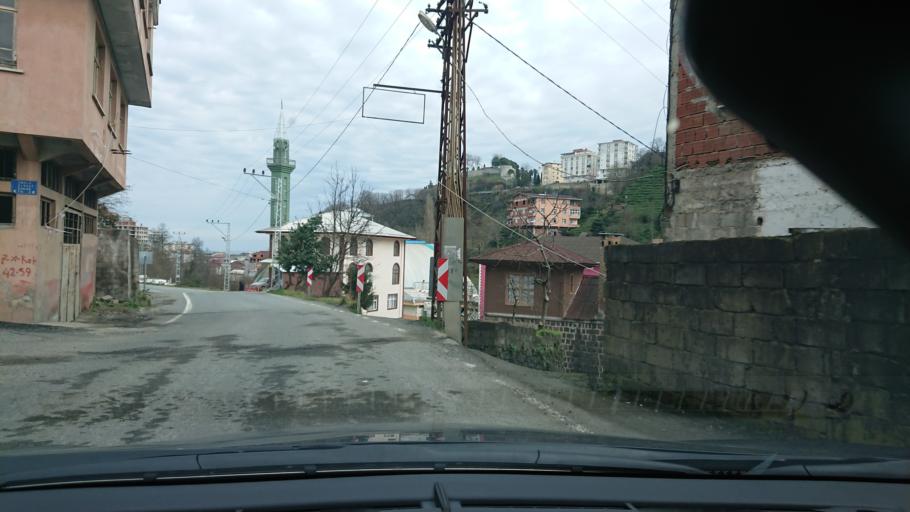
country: TR
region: Rize
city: Rize
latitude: 41.0257
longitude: 40.5047
